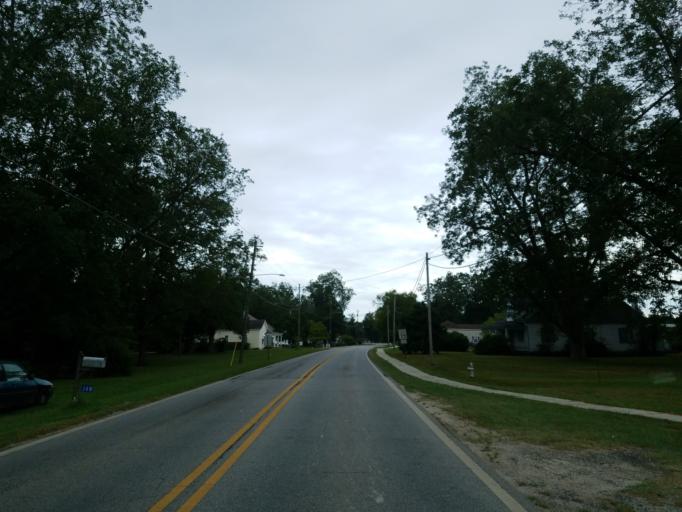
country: US
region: Georgia
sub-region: Lamar County
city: Barnesville
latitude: 33.1137
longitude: -84.1960
